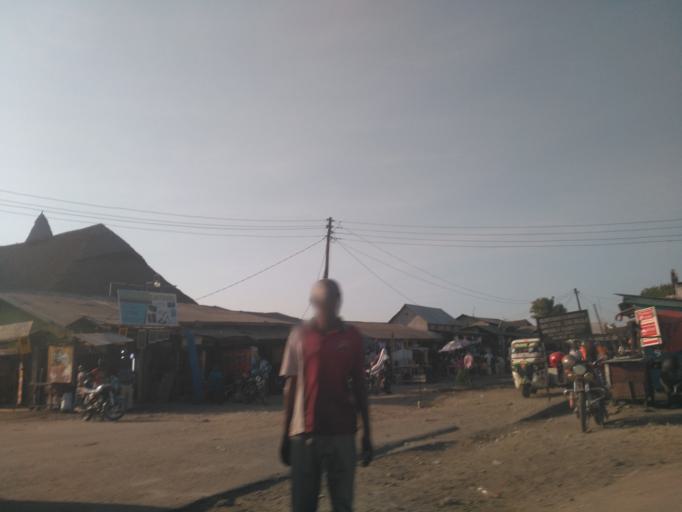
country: TZ
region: Pwani
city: Vikindu
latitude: -6.9218
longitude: 39.2701
